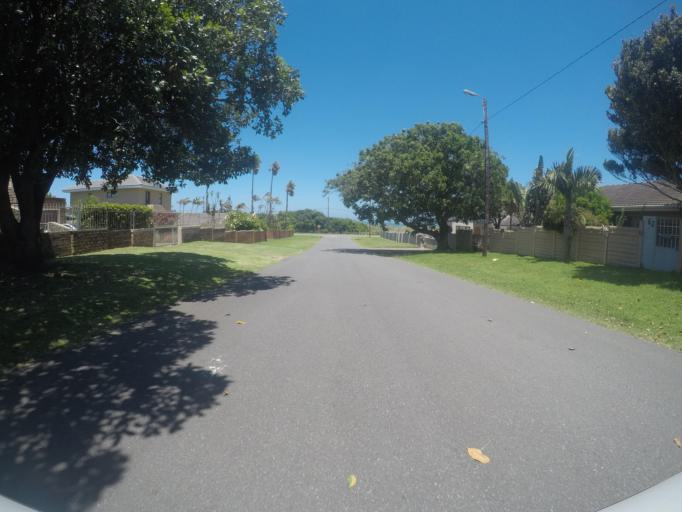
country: ZA
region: Eastern Cape
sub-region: Buffalo City Metropolitan Municipality
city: East London
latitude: -32.9503
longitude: 28.0123
